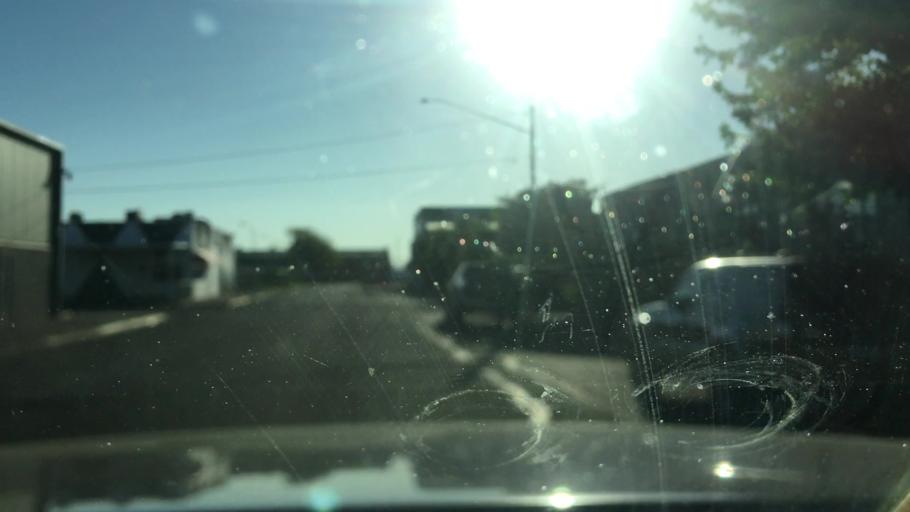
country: US
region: Oregon
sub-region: Lane County
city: Eugene
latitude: 44.0509
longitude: -123.1196
